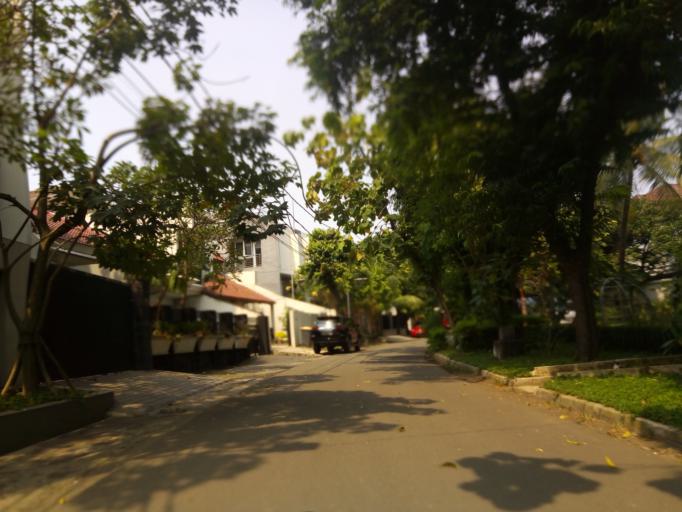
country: ID
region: Jakarta Raya
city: Jakarta
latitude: -6.2365
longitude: 106.7918
